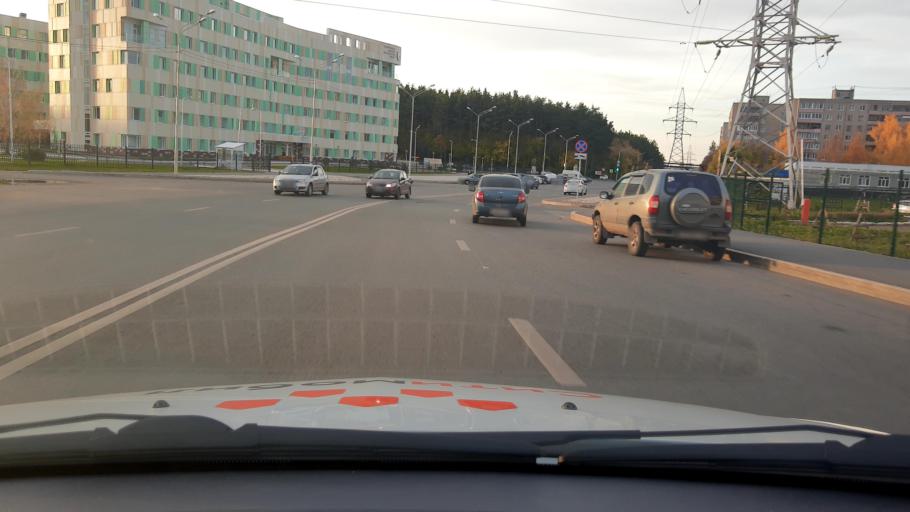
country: RU
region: Bashkortostan
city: Ufa
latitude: 54.7095
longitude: 56.0094
